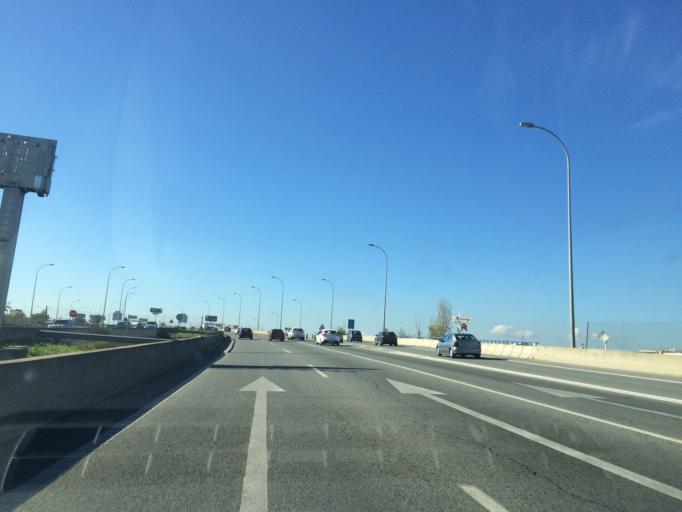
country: ES
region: Madrid
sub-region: Provincia de Madrid
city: Alcobendas
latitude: 40.5331
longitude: -3.6345
